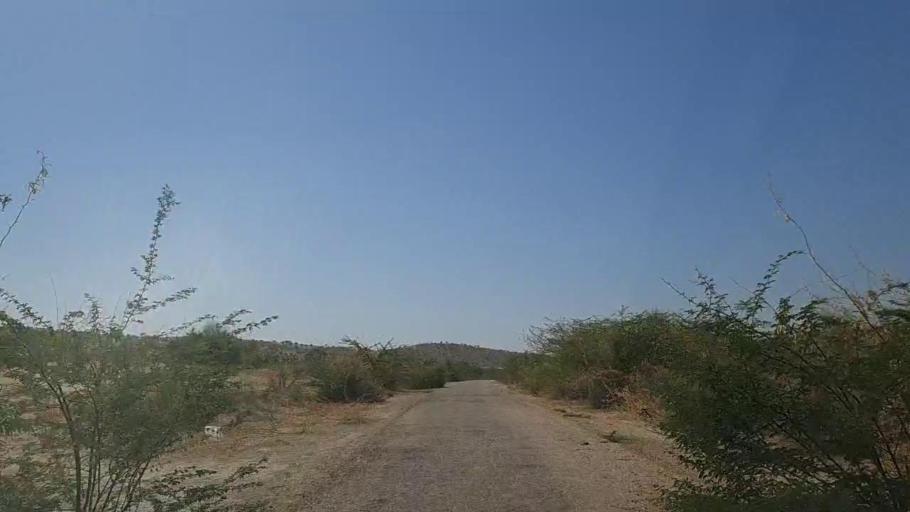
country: PK
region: Sindh
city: Mithi
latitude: 24.7997
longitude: 69.7159
